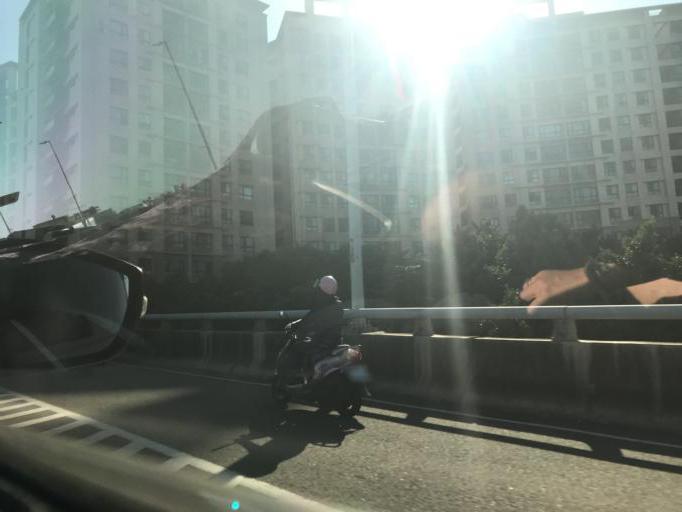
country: TW
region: Taiwan
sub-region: Hsinchu
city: Hsinchu
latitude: 24.8125
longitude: 120.9864
